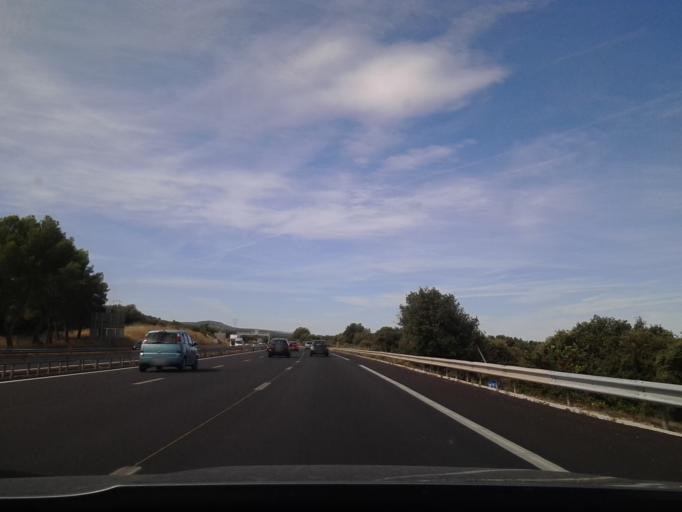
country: FR
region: Languedoc-Roussillon
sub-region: Departement de l'Herault
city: Fabregues
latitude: 43.5397
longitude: 3.7851
